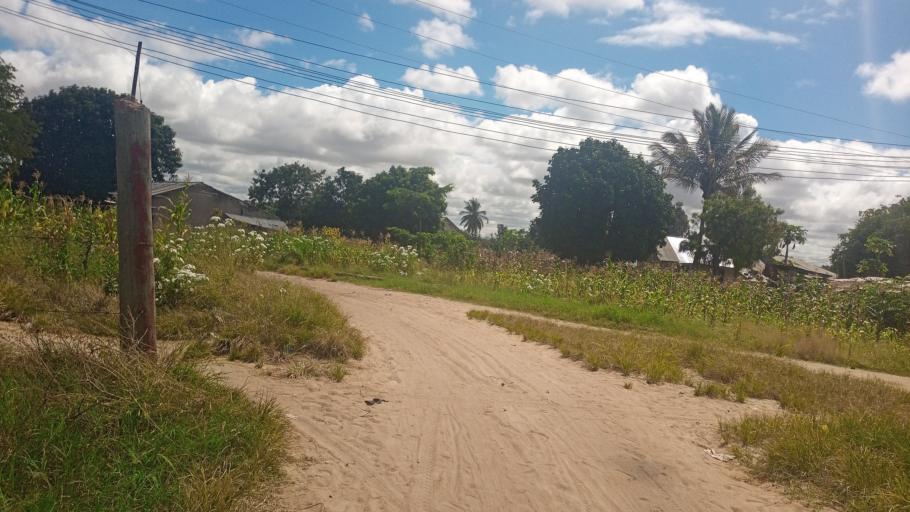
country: TZ
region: Dodoma
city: Dodoma
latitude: -6.1920
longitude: 35.7270
